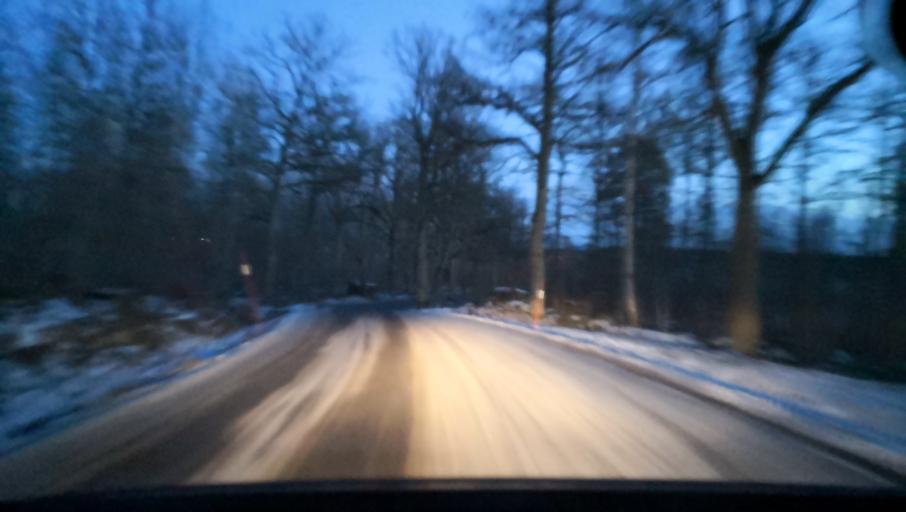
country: SE
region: Soedermanland
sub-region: Katrineholms Kommun
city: Katrineholm
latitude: 59.0713
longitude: 16.3376
